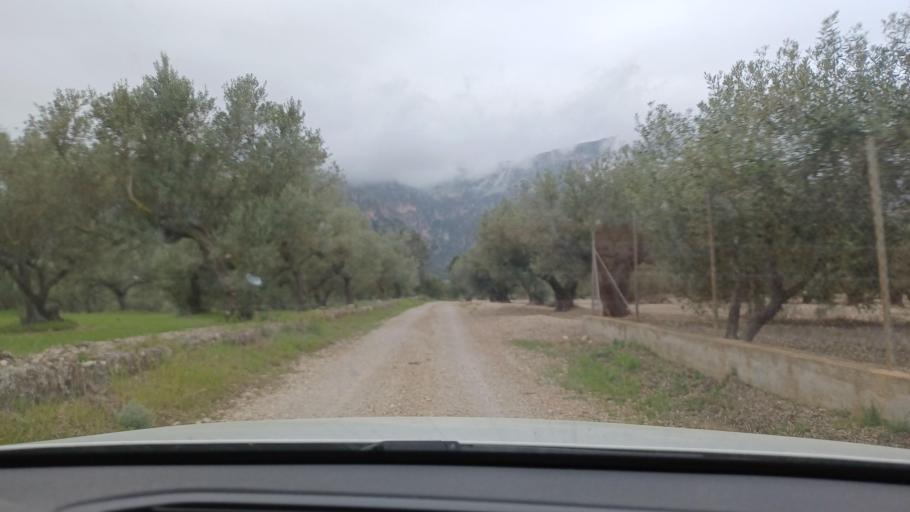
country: ES
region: Catalonia
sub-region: Provincia de Tarragona
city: Mas de Barberans
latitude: 40.8052
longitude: 0.4099
